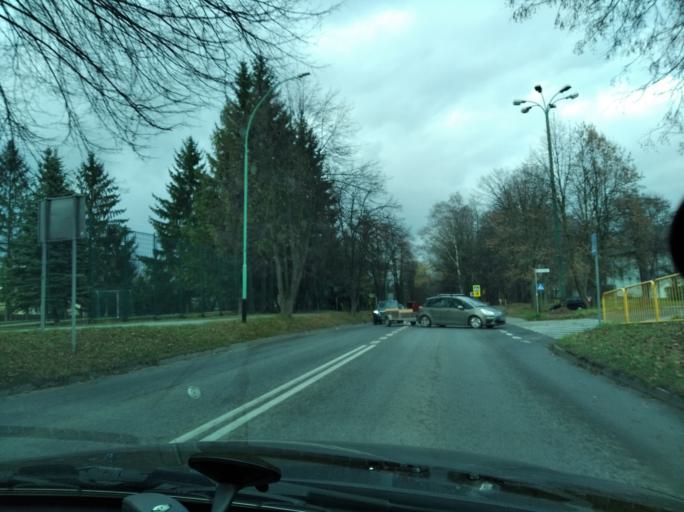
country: PL
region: Subcarpathian Voivodeship
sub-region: Powiat lancucki
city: Lancut
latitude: 50.0718
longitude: 22.2372
